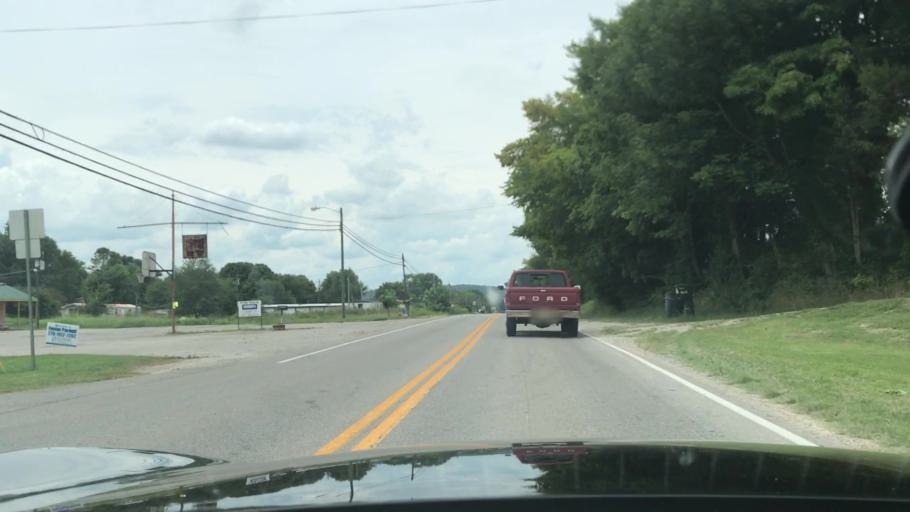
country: US
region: Kentucky
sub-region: Hart County
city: Horse Cave
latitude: 37.1772
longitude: -85.8785
